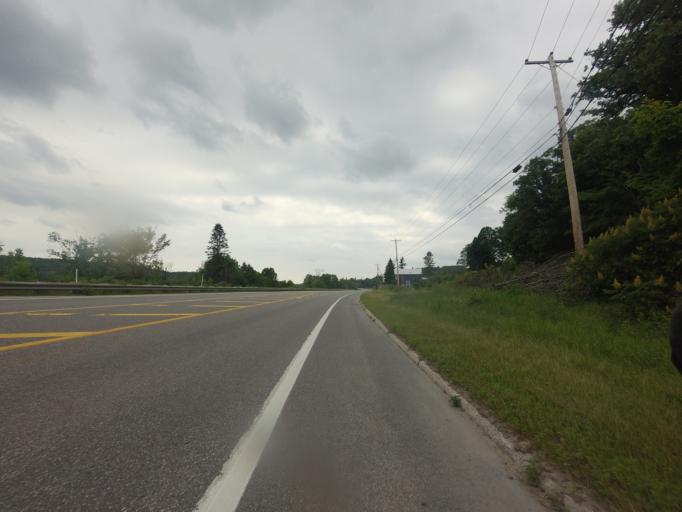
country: CA
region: Quebec
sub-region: Outaouais
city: Wakefield
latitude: 45.7191
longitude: -75.9135
